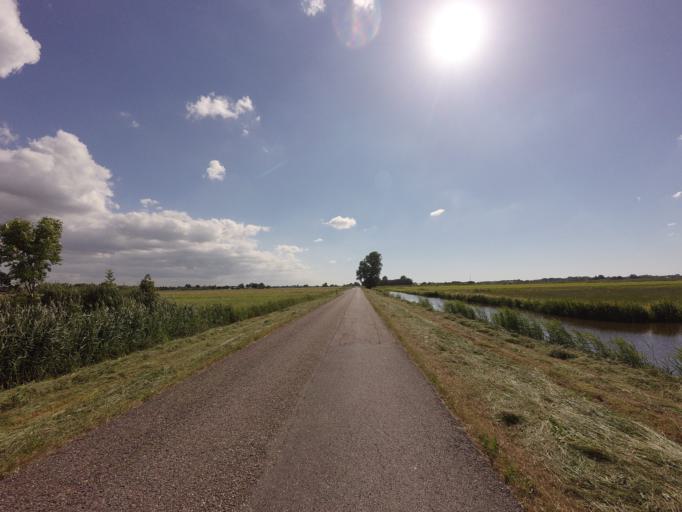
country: NL
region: Utrecht
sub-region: Gemeente De Ronde Venen
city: Mijdrecht
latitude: 52.2295
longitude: 4.8665
